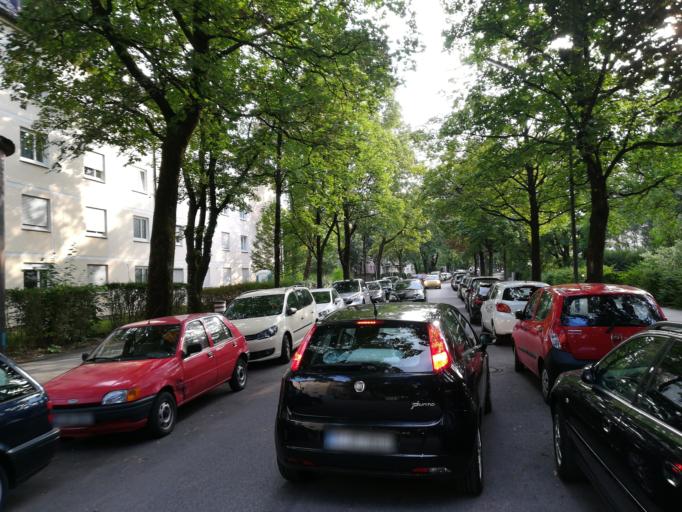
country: DE
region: Bavaria
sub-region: Upper Bavaria
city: Munich
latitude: 48.1645
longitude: 11.5324
